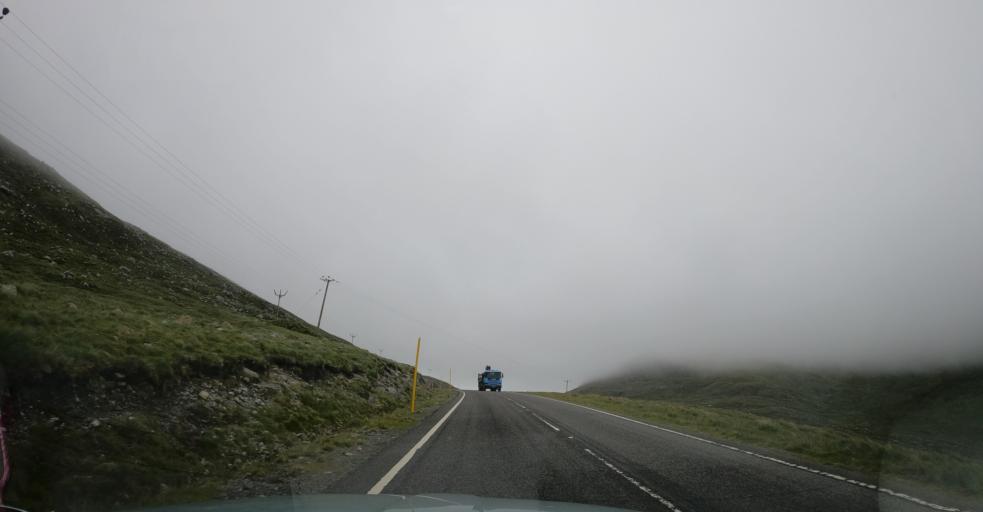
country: GB
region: Scotland
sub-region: Eilean Siar
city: Harris
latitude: 57.9451
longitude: -6.8078
